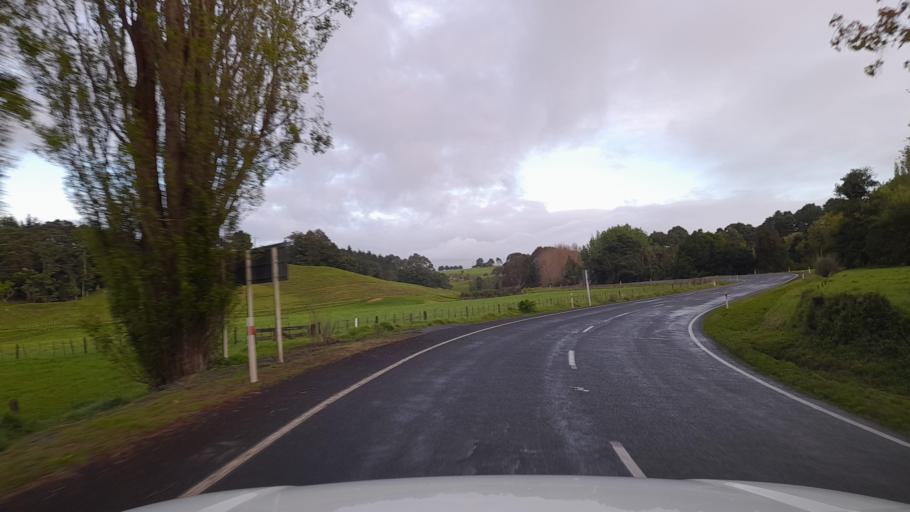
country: NZ
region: Northland
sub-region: Kaipara District
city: Dargaville
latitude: -35.7001
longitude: 173.9135
